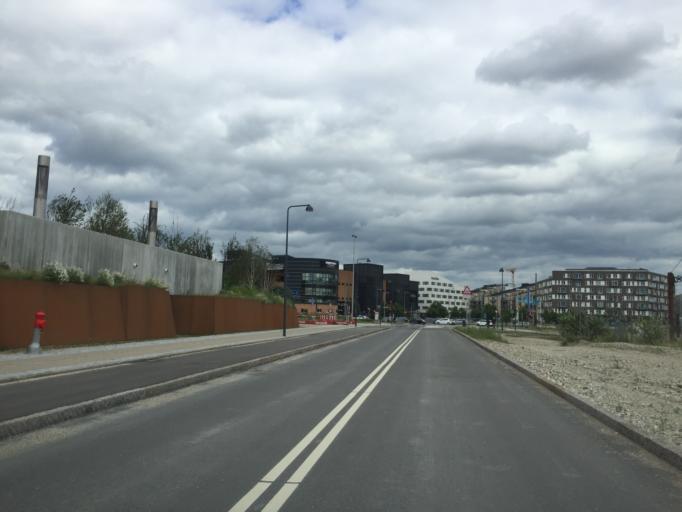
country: DK
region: Capital Region
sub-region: Kobenhavn
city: Copenhagen
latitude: 55.6619
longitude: 12.5562
